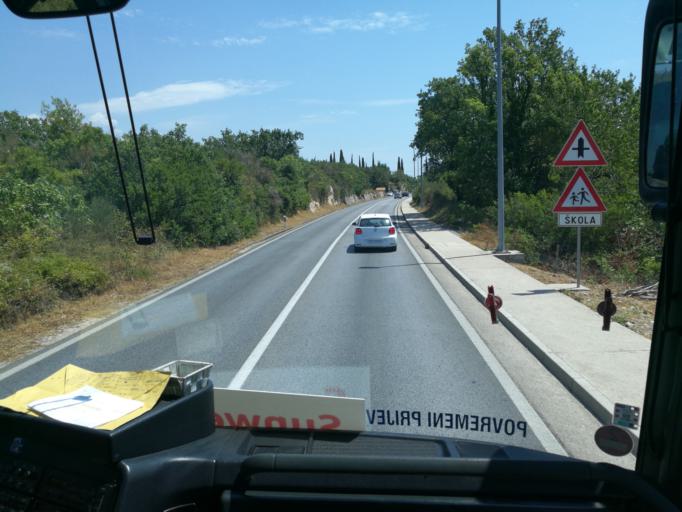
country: HR
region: Dubrovacko-Neretvanska
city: Jasenice
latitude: 42.5636
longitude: 18.2503
